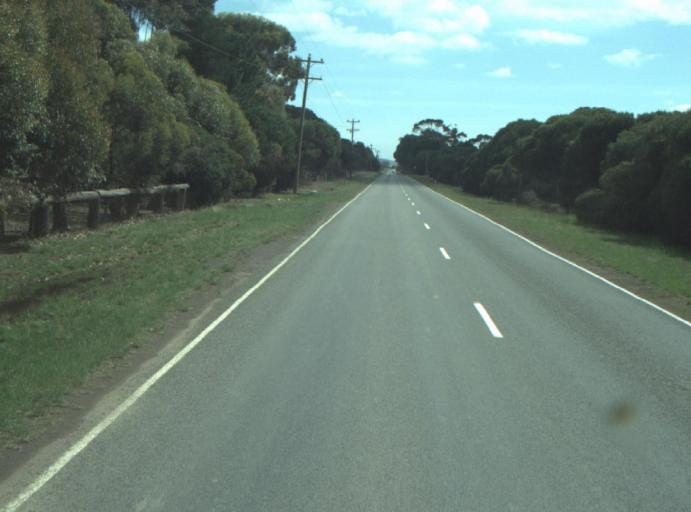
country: AU
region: Victoria
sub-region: Greater Geelong
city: Lara
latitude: -38.0451
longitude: 144.4295
